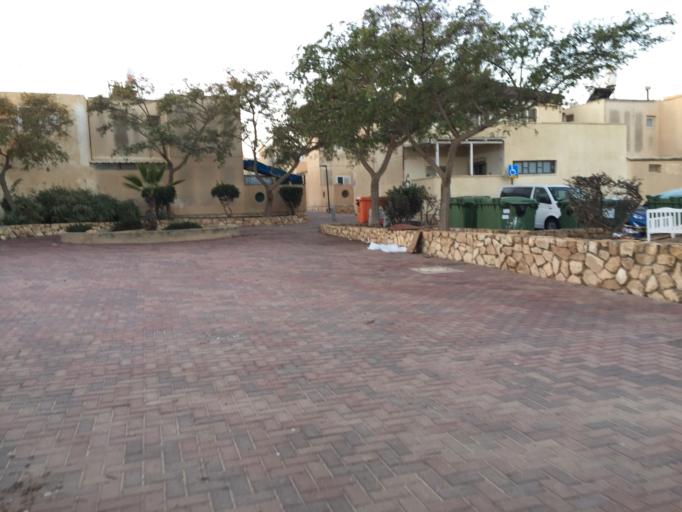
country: IL
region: Southern District
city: Mitzpe Ramon
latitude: 30.6127
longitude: 34.8013
